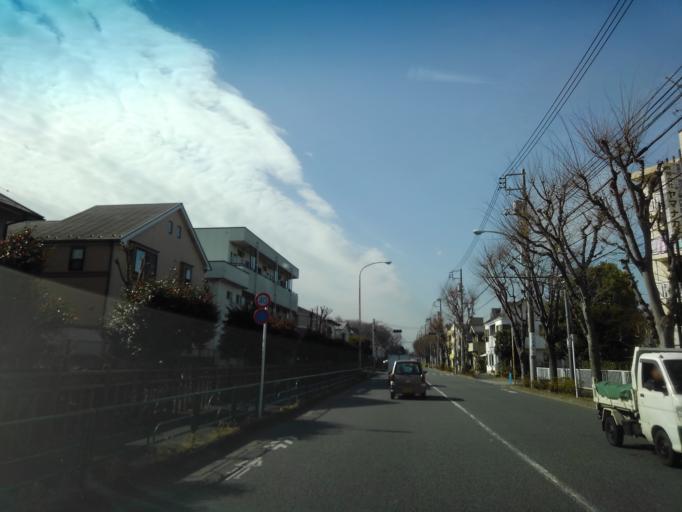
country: JP
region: Tokyo
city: Tanashicho
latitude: 35.7651
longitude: 139.5147
